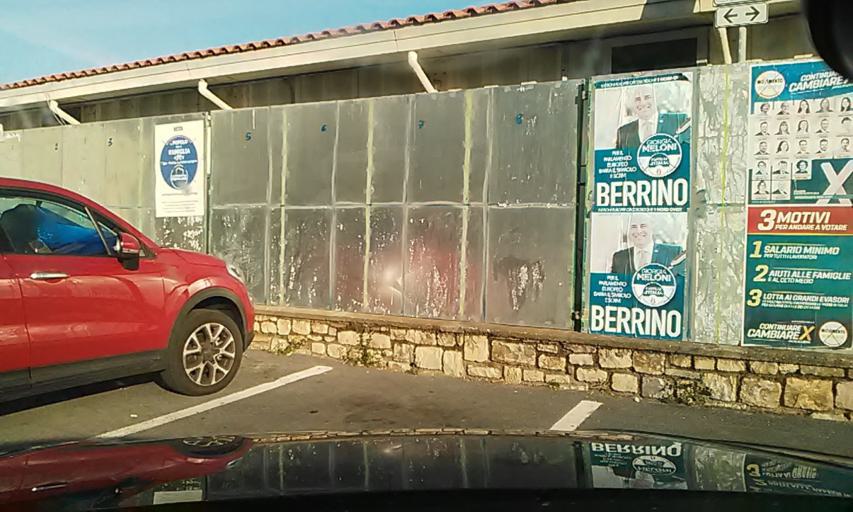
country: IT
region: Liguria
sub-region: Provincia di Savona
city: Marina di Andora
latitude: 43.9520
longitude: 8.1544
